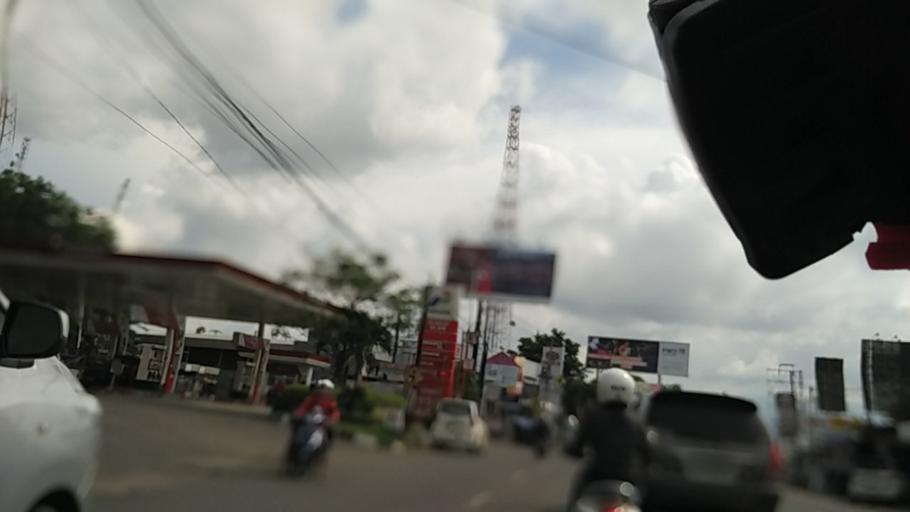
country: ID
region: Central Java
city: Semarang
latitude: -7.0424
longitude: 110.4222
